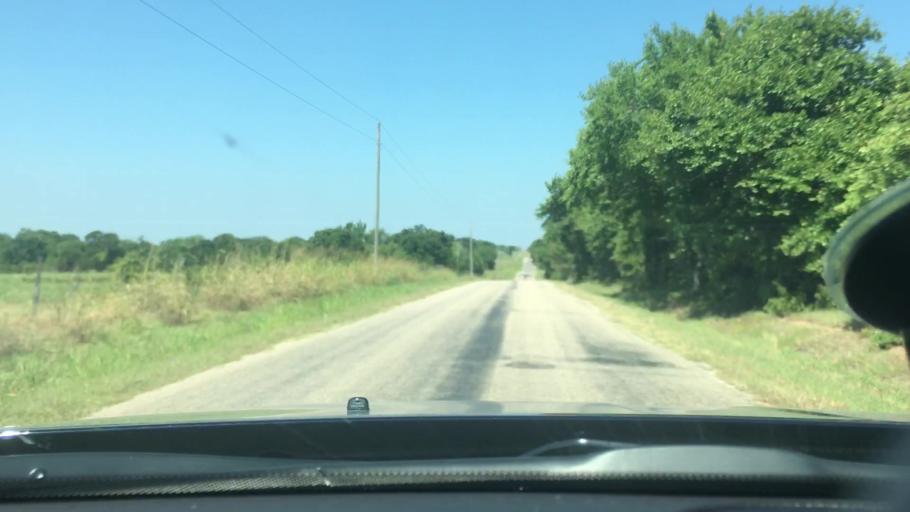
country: US
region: Oklahoma
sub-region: Johnston County
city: Tishomingo
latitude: 34.3177
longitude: -96.6631
